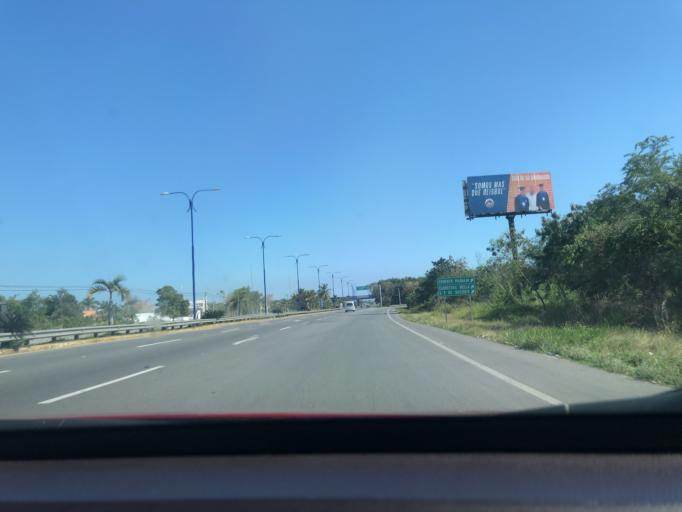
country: DO
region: Santo Domingo
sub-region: Santo Domingo
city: Boca Chica
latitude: 18.4529
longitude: -69.5990
